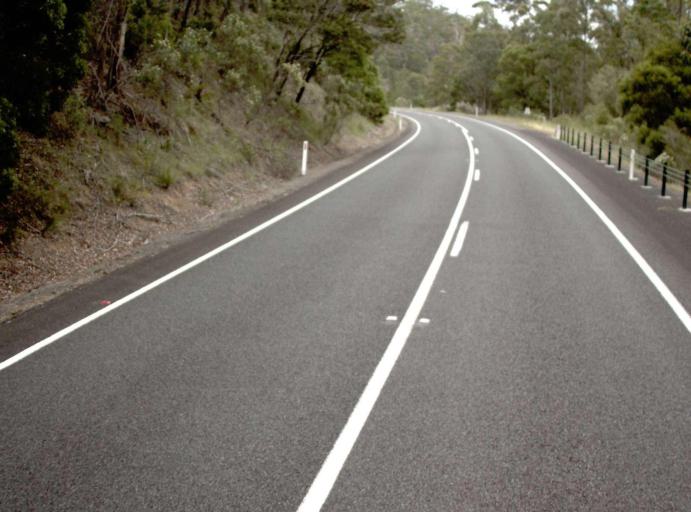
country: AU
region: New South Wales
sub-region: Bombala
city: Bombala
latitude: -37.2613
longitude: 149.2360
